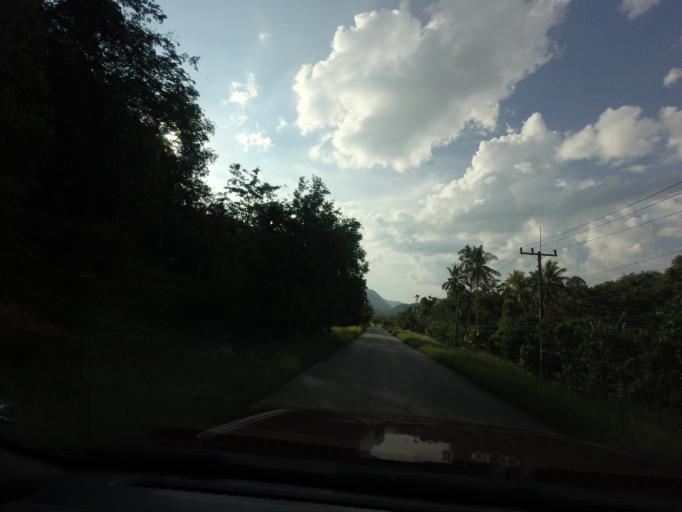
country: TH
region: Yala
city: Ban Nang Sata
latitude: 6.2185
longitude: 101.2308
